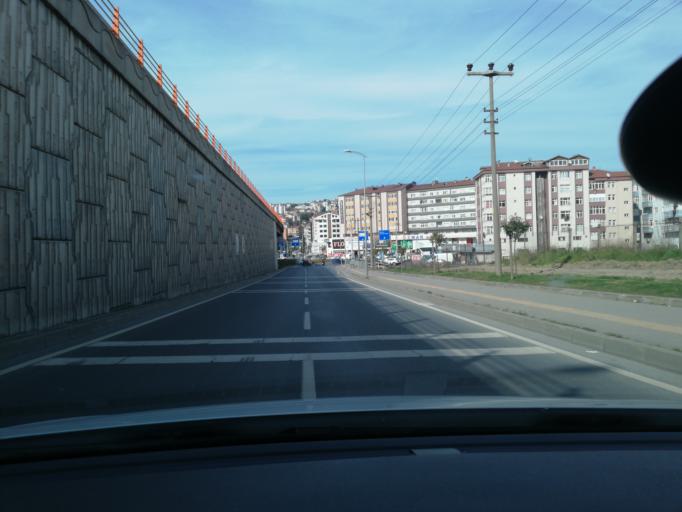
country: TR
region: Zonguldak
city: Eregli
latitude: 41.2682
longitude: 31.4354
